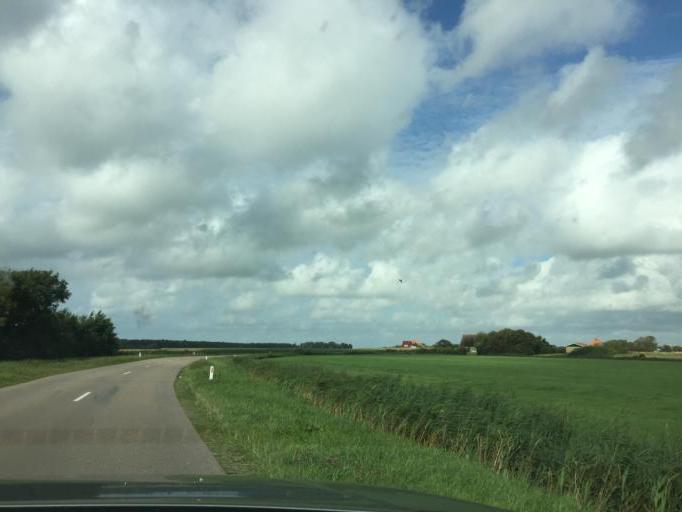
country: NL
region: North Holland
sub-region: Gemeente Texel
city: Den Burg
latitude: 53.0442
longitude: 4.7494
